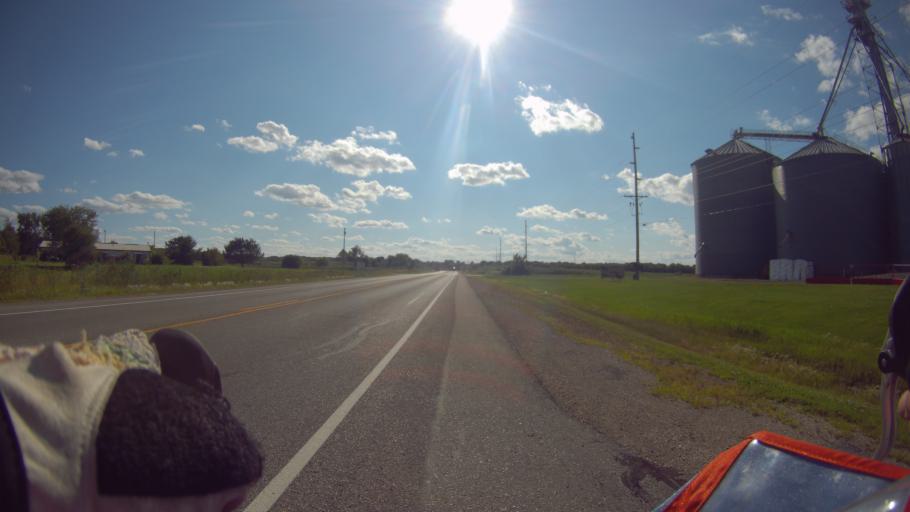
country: US
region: Wisconsin
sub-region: Dane County
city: Oregon
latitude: 42.9178
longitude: -89.3611
